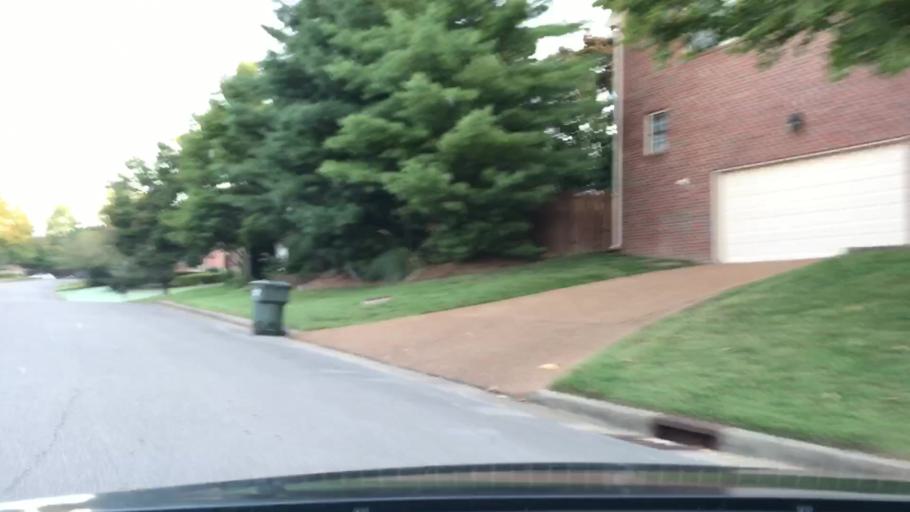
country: US
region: Tennessee
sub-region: Williamson County
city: Brentwood Estates
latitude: 36.0169
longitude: -86.7351
